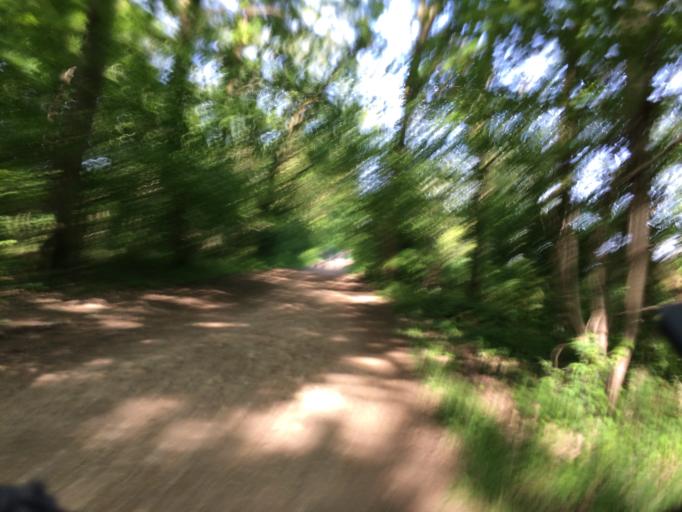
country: FR
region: Ile-de-France
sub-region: Departement des Hauts-de-Seine
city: Chatenay-Malabry
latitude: 48.7583
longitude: 2.2597
